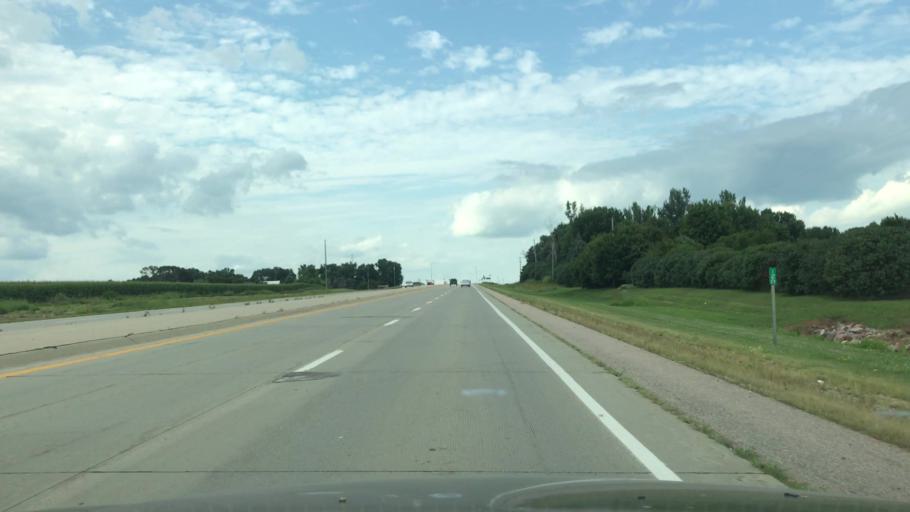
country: US
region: Iowa
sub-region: Plymouth County
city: Le Mars
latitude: 42.8111
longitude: -96.1747
